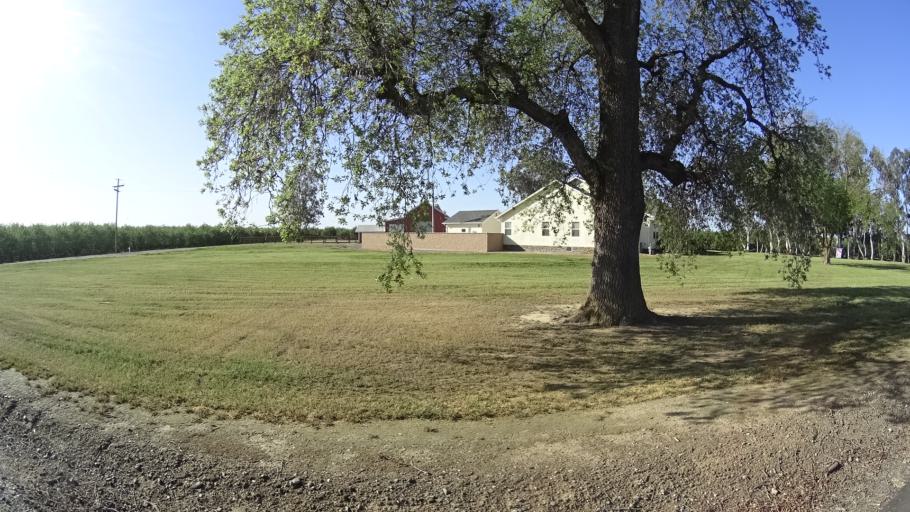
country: US
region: California
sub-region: Glenn County
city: Orland
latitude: 39.6959
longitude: -122.1142
